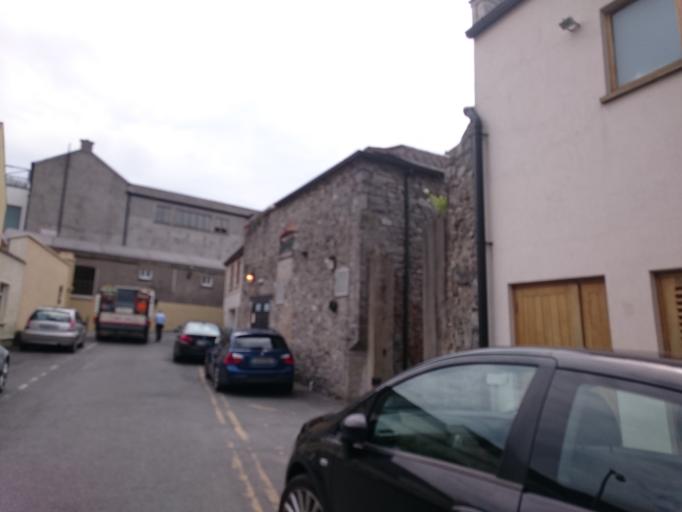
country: IE
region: Leinster
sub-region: Kilkenny
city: Kilkenny
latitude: 52.6549
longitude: -7.2541
